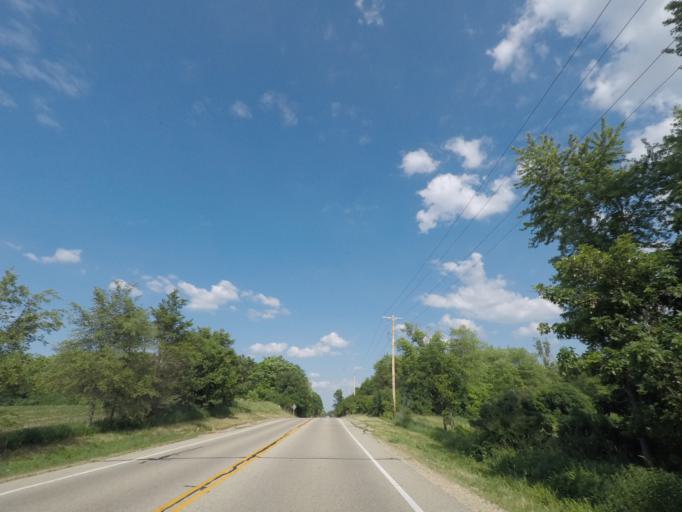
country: US
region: Wisconsin
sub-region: Walworth County
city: East Troy
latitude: 42.7932
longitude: -88.4906
